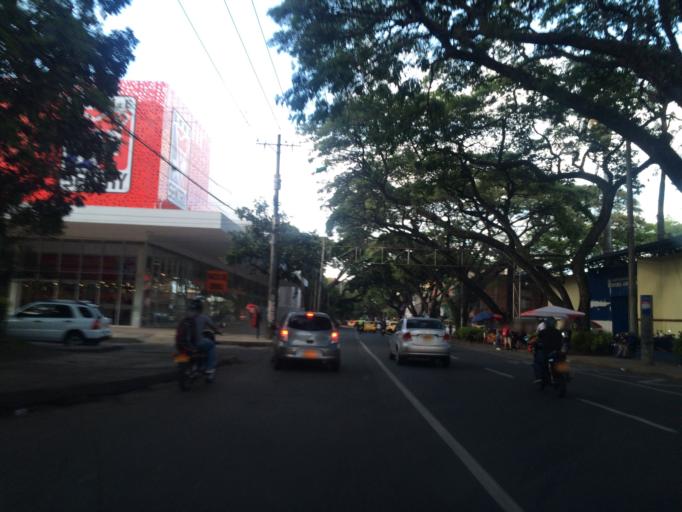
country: CO
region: Valle del Cauca
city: Cali
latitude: 3.4702
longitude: -76.5279
